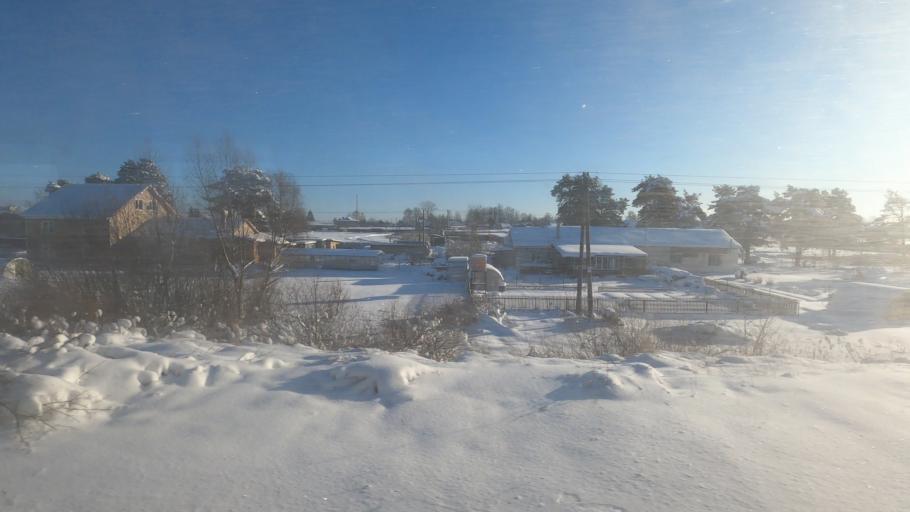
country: RU
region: Moskovskaya
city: Orud'yevo
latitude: 56.4424
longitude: 37.5145
